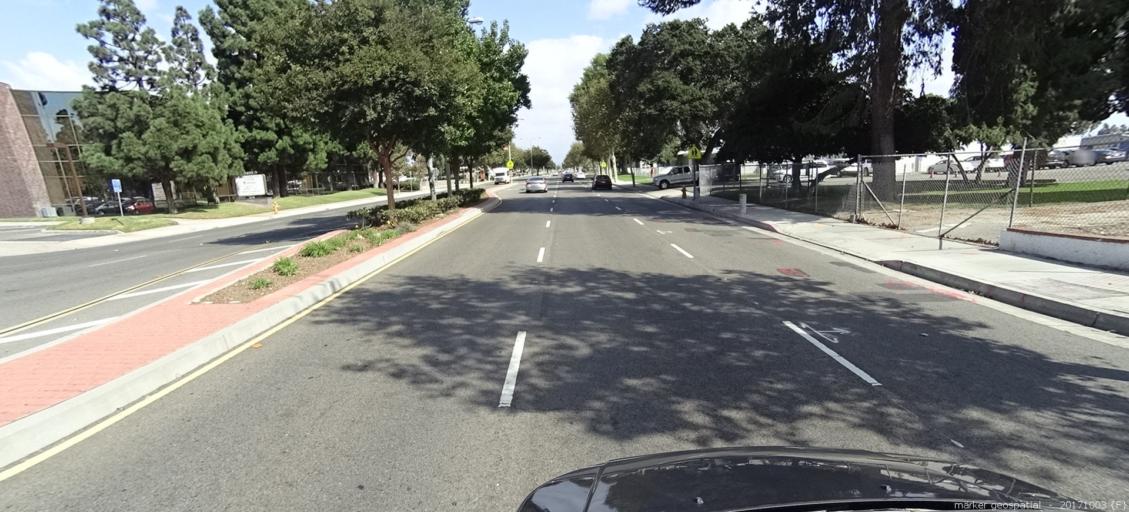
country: US
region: California
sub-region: Orange County
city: Garden Grove
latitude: 33.7742
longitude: -117.9368
